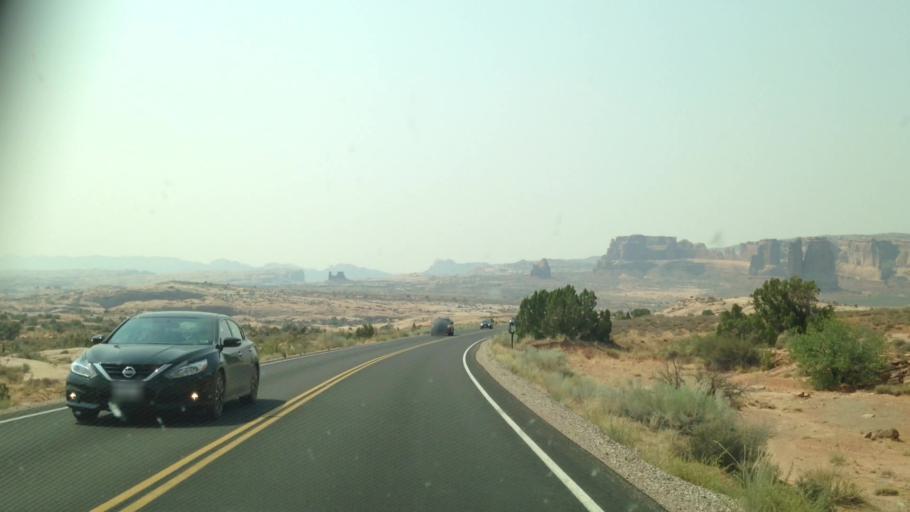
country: US
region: Utah
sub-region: Grand County
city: Moab
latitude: 38.6595
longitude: -109.5879
